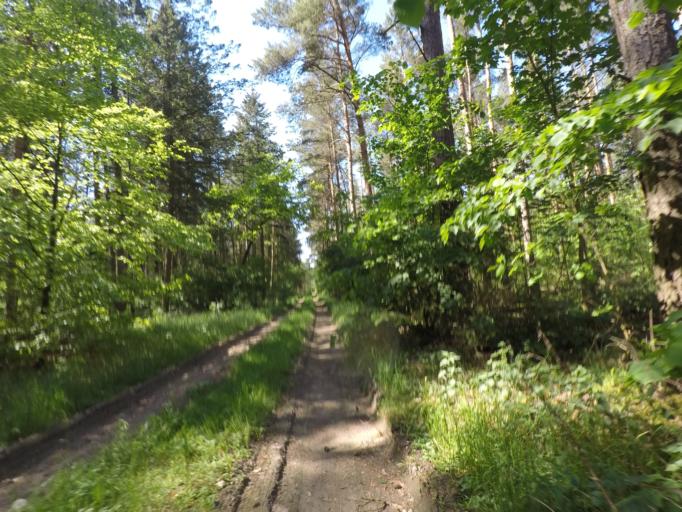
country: DE
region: Brandenburg
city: Melchow
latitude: 52.8230
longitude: 13.7506
